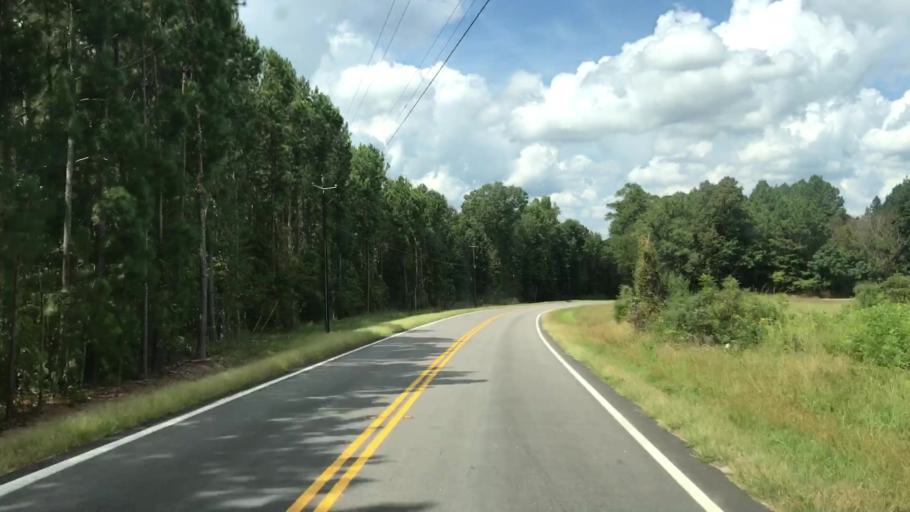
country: US
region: Georgia
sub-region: Greene County
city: Greensboro
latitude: 33.5596
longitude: -83.1357
